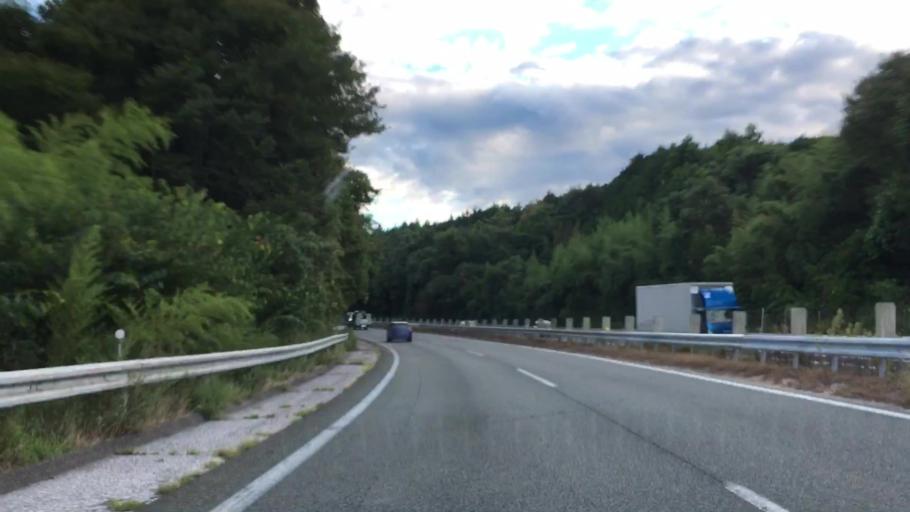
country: JP
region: Yamaguchi
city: Ogori-shimogo
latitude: 34.1685
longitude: 131.2416
